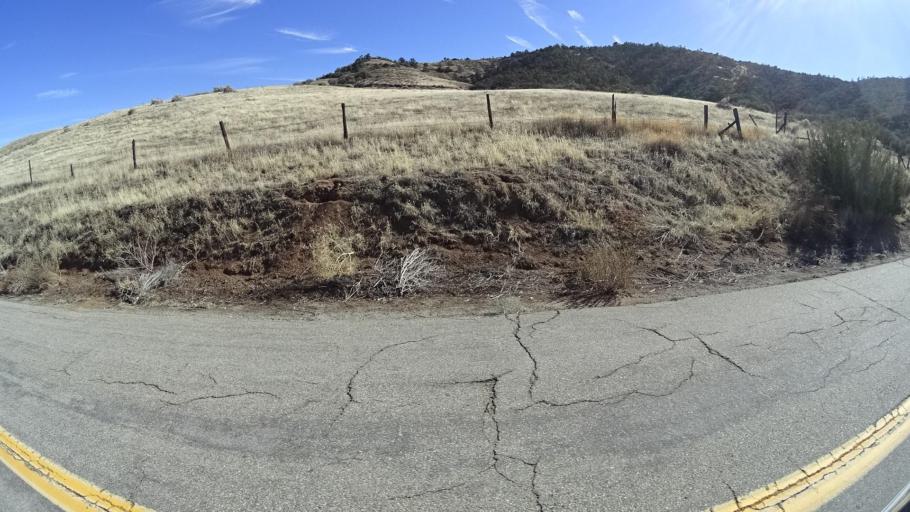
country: US
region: California
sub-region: Kern County
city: Maricopa
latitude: 34.8806
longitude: -119.3562
